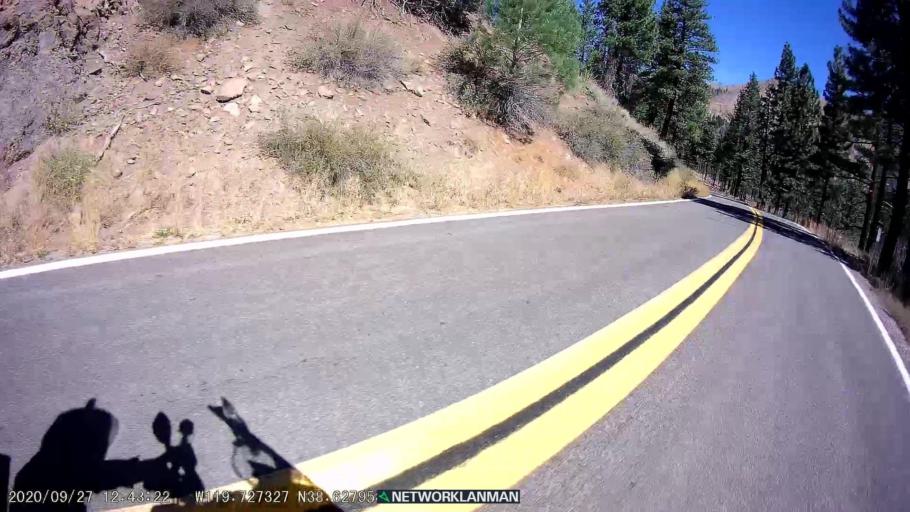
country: US
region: Nevada
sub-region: Douglas County
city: Gardnerville Ranchos
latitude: 38.6280
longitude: -119.7270
